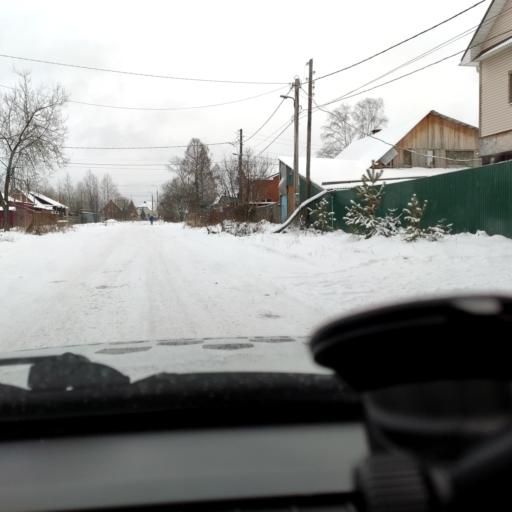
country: RU
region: Perm
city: Perm
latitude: 58.0609
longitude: 56.3658
